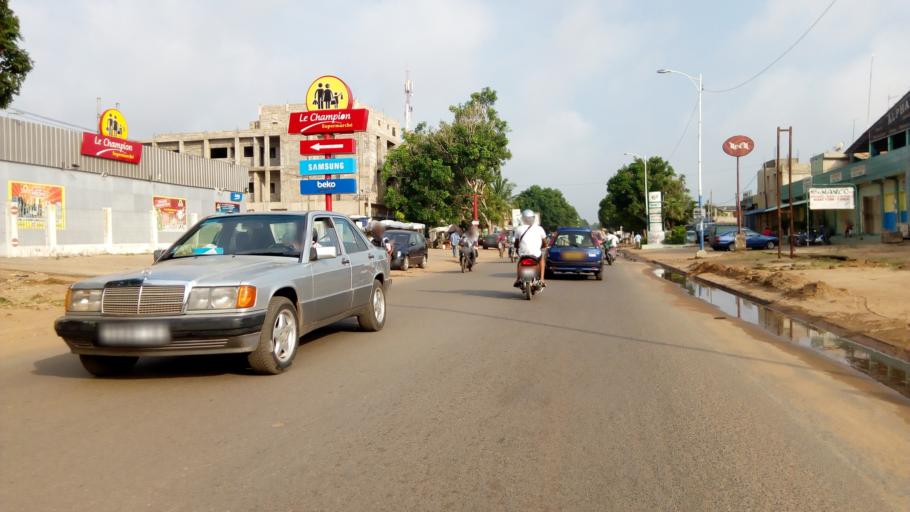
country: TG
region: Maritime
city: Lome
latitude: 6.1785
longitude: 1.1757
